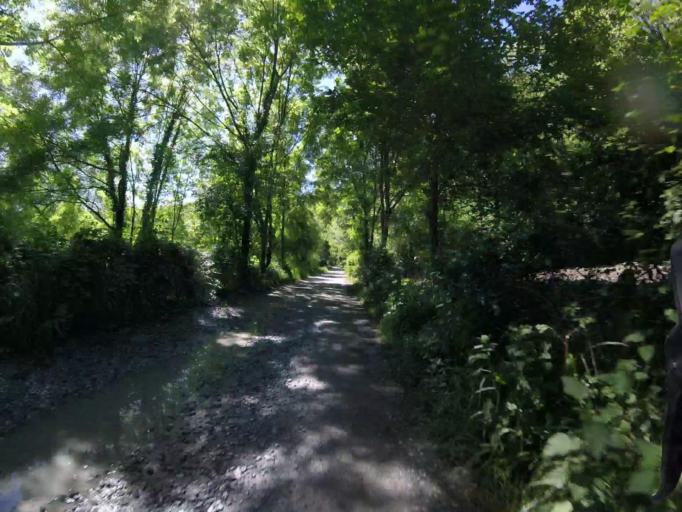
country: ES
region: Navarre
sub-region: Provincia de Navarra
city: Bera
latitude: 43.2796
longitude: -1.7140
